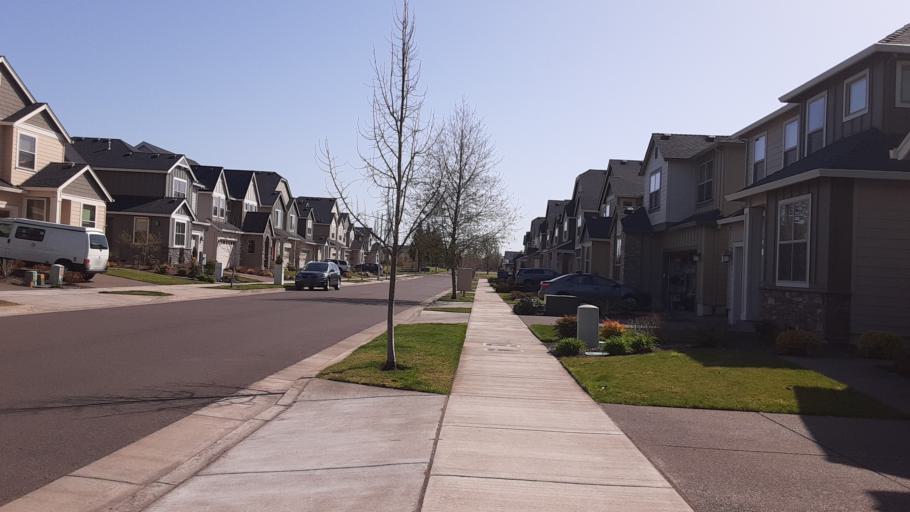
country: US
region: Oregon
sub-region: Benton County
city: Corvallis
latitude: 44.5324
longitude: -123.2607
